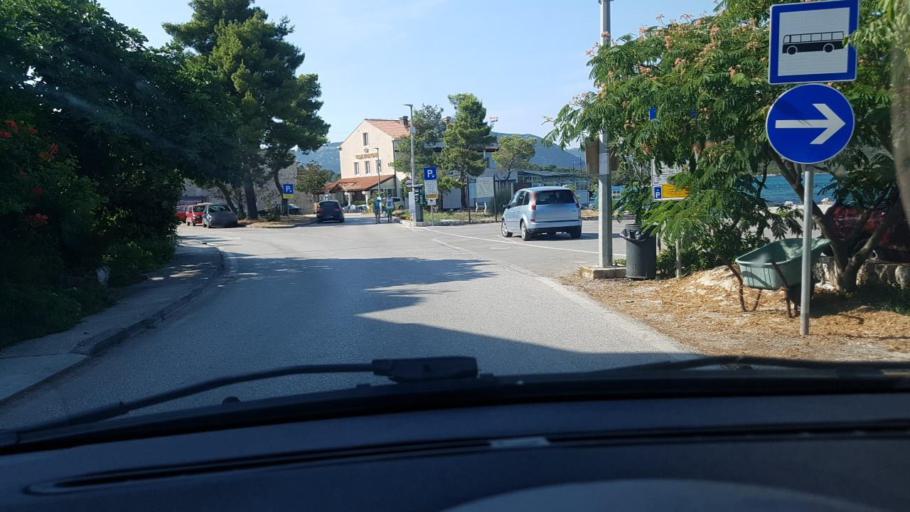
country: HR
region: Dubrovacko-Neretvanska
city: Ston
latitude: 42.8458
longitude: 17.7053
